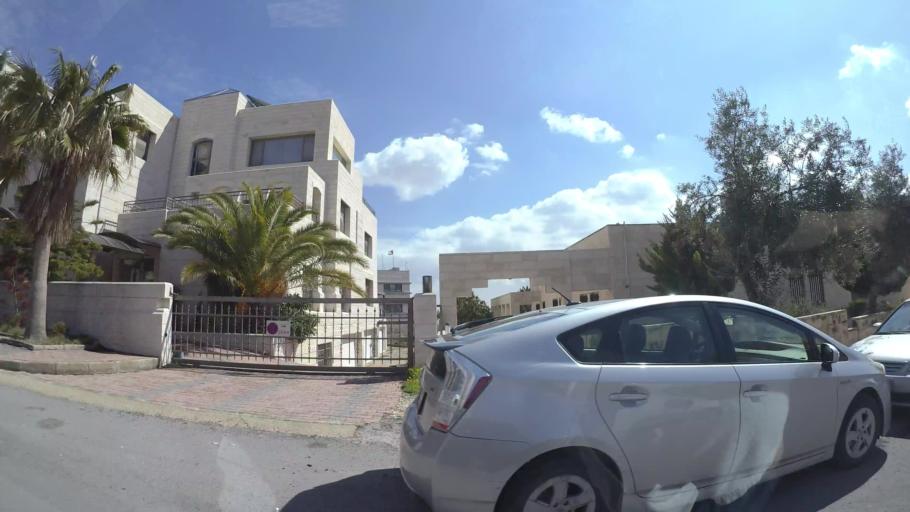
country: JO
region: Amman
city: Amman
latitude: 31.9910
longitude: 35.9059
